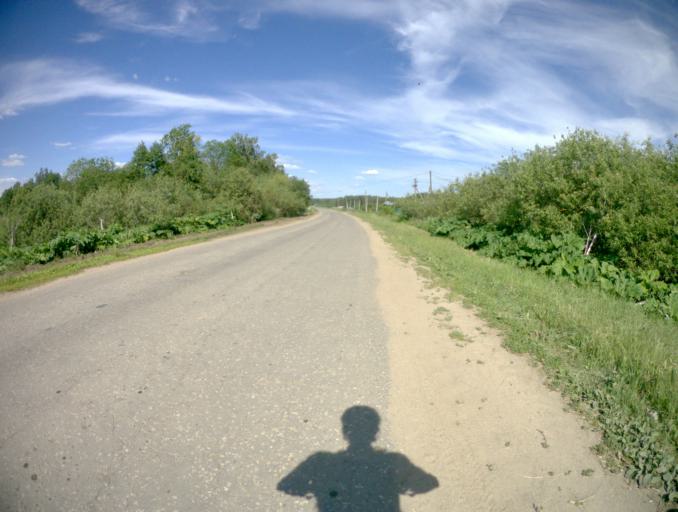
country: RU
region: Vladimir
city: Stavrovo
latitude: 56.1478
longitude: 40.0484
